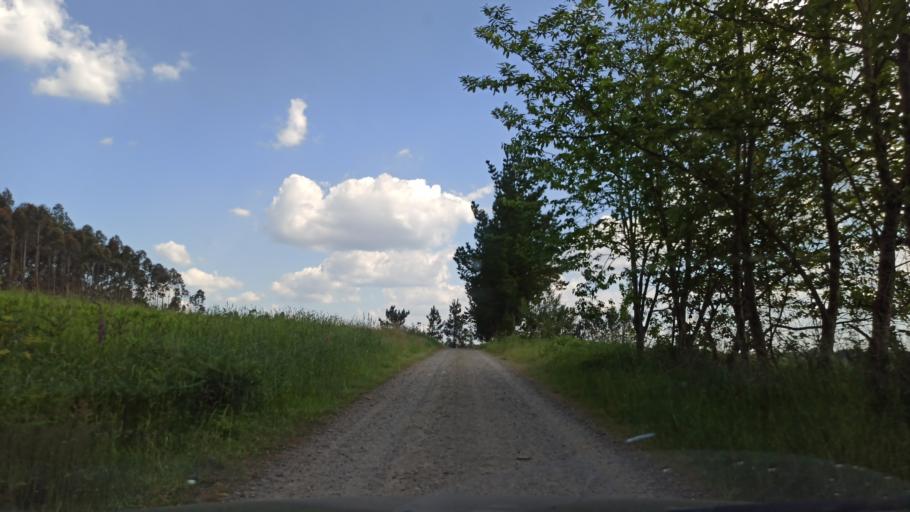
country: ES
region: Galicia
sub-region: Provincia da Coruna
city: Santa Comba
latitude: 43.0753
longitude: -8.7163
